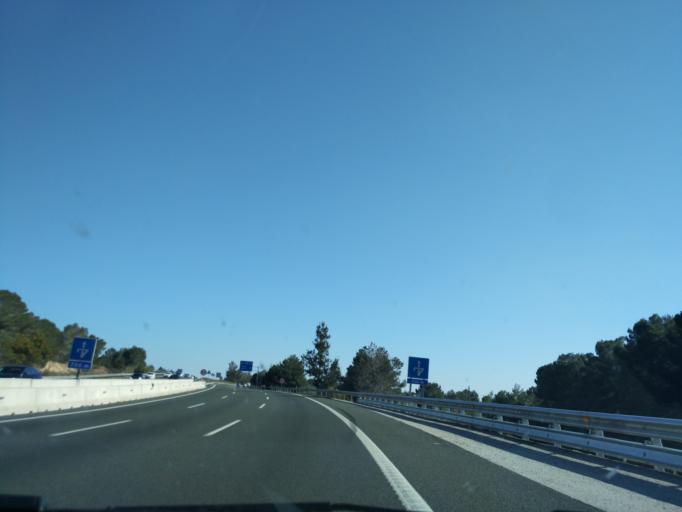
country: ES
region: Murcia
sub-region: Murcia
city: Murcia
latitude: 37.8927
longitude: -1.1427
